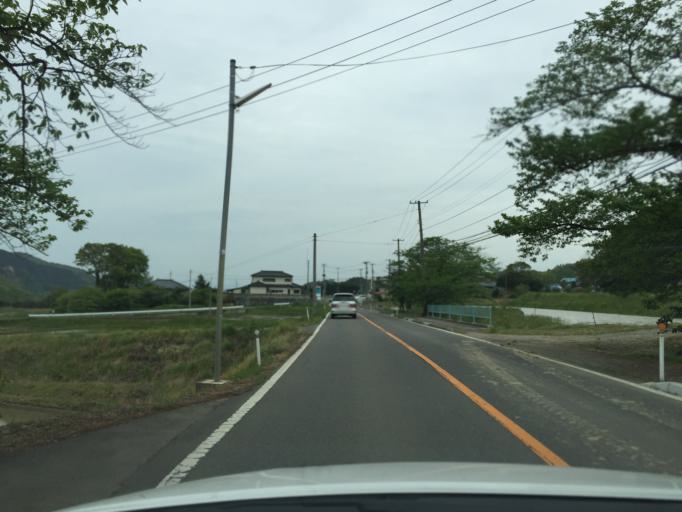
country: JP
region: Fukushima
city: Motomiya
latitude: 37.4994
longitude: 140.2784
